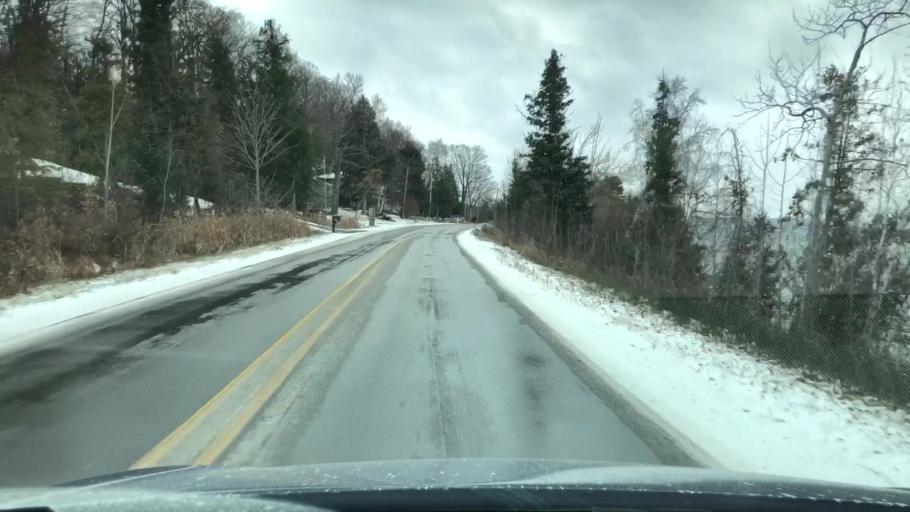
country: US
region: Michigan
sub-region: Leelanau County
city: Greilickville
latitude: 44.8405
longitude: -85.5596
